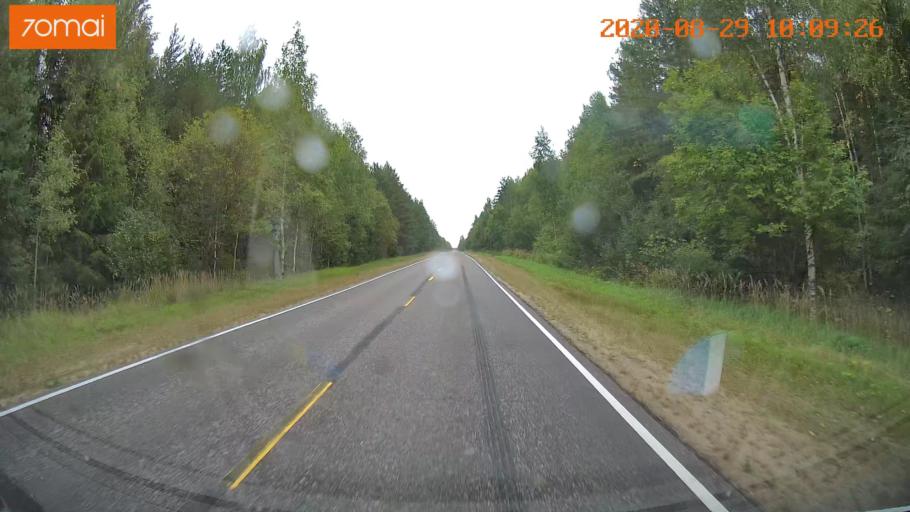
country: RU
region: Ivanovo
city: Kuznechikha
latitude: 57.3752
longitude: 42.6261
